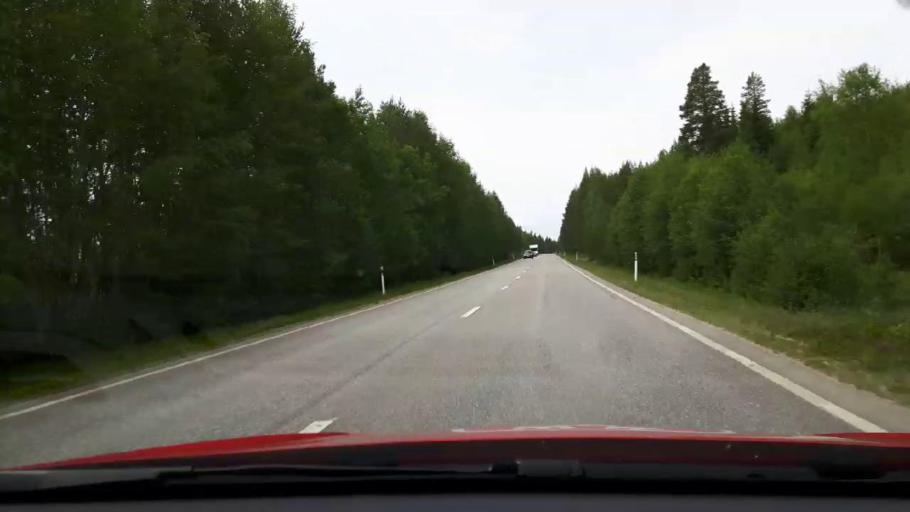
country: SE
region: Jaemtland
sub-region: Harjedalens Kommun
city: Sveg
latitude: 62.0997
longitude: 14.2198
